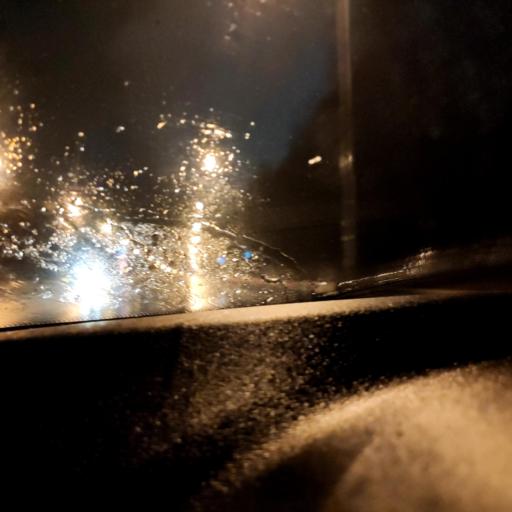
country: RU
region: Samara
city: Petra-Dubrava
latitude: 53.2866
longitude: 50.2500
